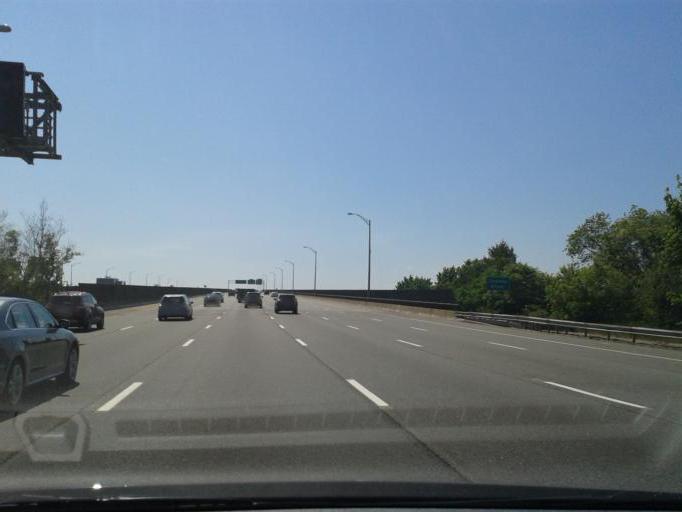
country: US
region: Connecticut
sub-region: New London County
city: Groton
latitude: 41.3647
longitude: -72.0788
